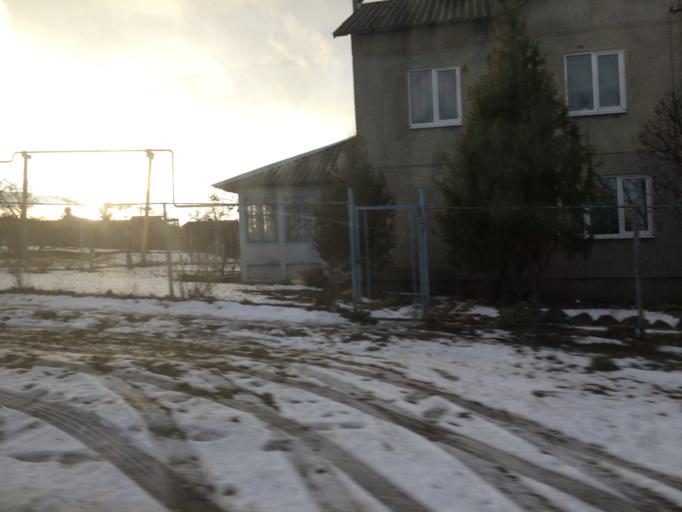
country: RU
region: Tula
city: Cherepet'
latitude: 54.1123
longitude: 36.3270
